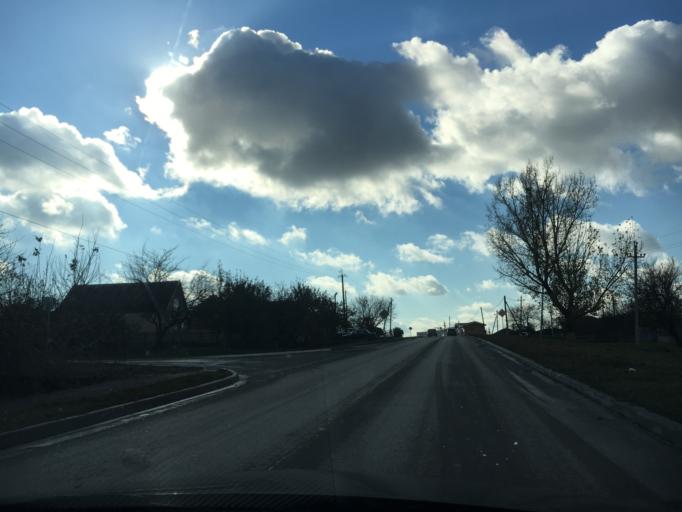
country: RU
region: Rostov
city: Matveyev Kurgan
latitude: 47.5605
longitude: 38.8723
